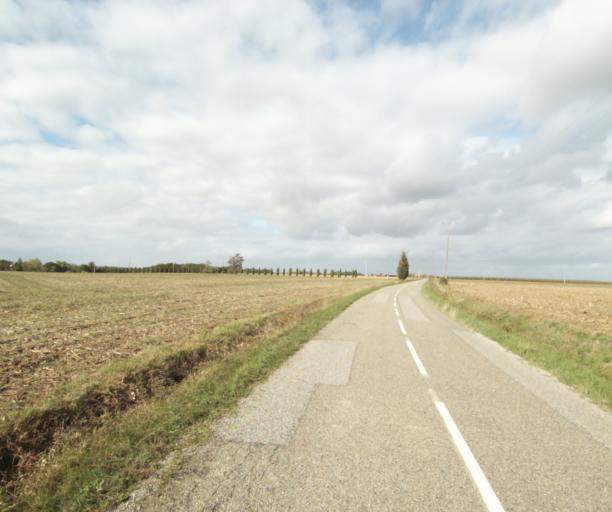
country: FR
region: Midi-Pyrenees
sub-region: Departement du Tarn-et-Garonne
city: Finhan
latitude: 43.9038
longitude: 1.1465
